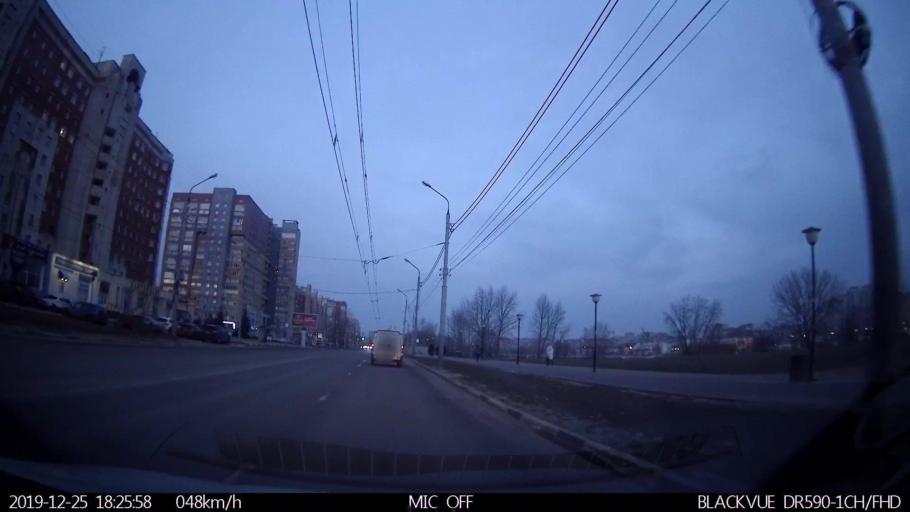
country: RU
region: Nizjnij Novgorod
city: Nizhniy Novgorod
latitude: 56.3346
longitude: 43.9446
